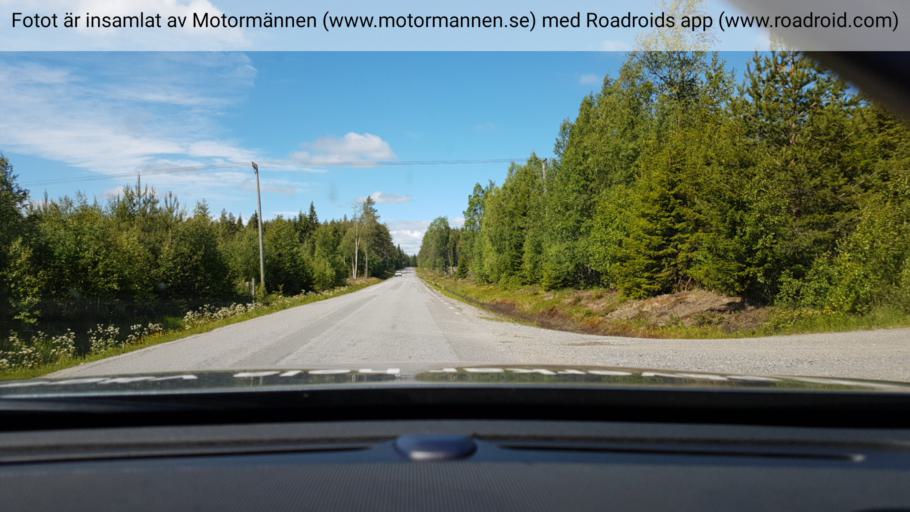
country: SE
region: Vaesterbotten
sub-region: Skelleftea Kommun
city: Burea
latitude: 64.4539
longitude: 21.4378
